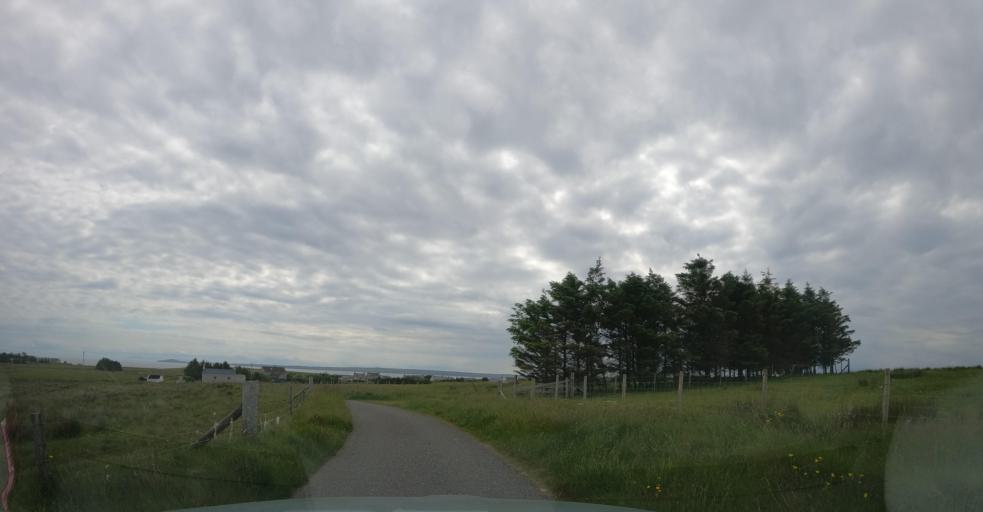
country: GB
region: Scotland
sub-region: Eilean Siar
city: Isle of Lewis
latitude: 58.2726
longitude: -6.3005
